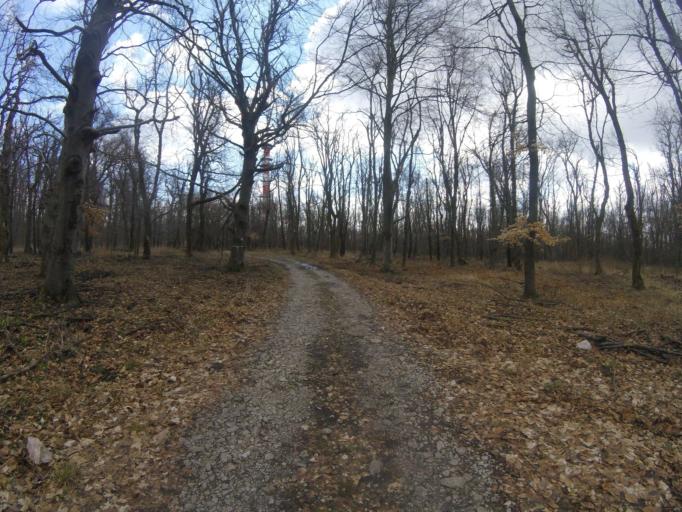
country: HU
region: Komarom-Esztergom
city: Tardos
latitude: 47.6779
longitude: 18.4909
